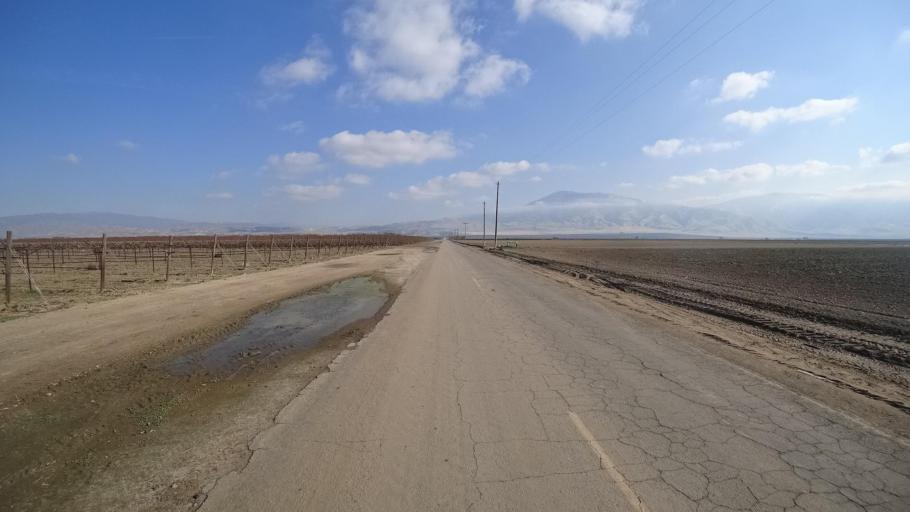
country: US
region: California
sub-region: Kern County
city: Arvin
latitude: 35.2531
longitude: -118.8029
